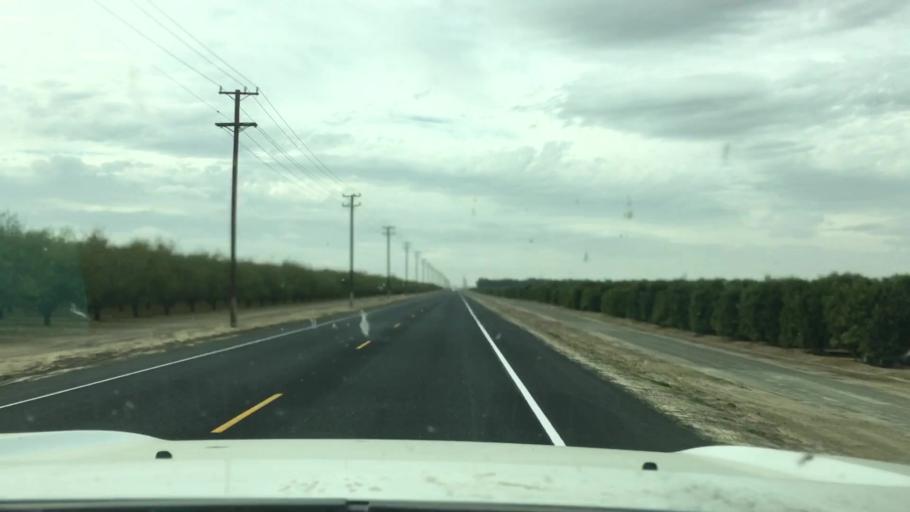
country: US
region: California
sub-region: Kern County
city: Lost Hills
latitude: 35.4992
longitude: -119.7262
